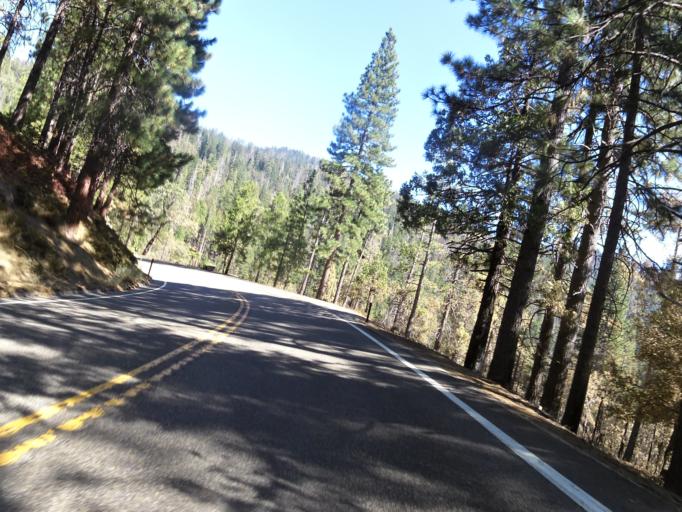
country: US
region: California
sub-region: Mariposa County
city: Yosemite Valley
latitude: 37.5798
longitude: -119.6811
